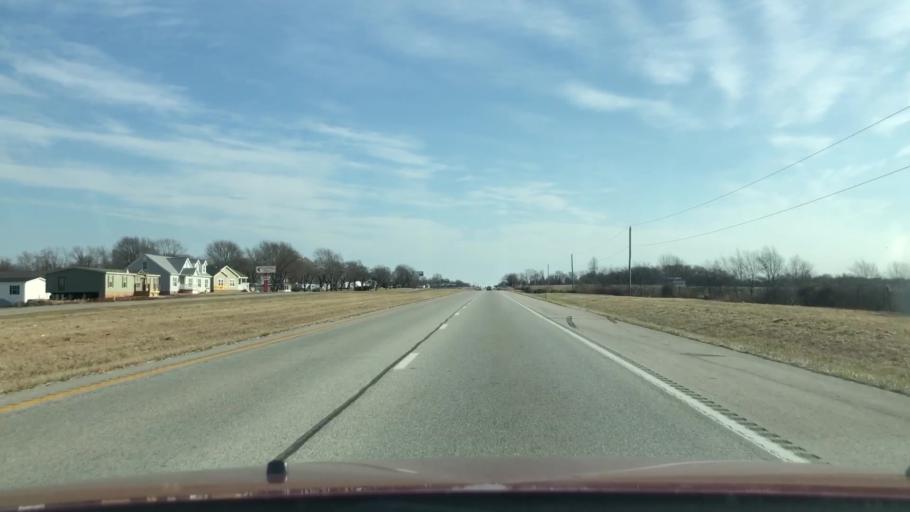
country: US
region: Missouri
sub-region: Webster County
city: Rogersville
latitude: 37.1187
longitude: -93.1339
